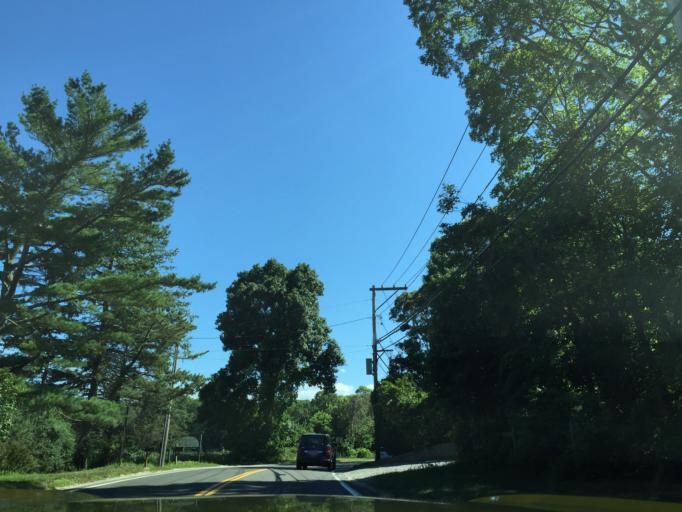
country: US
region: New York
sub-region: Suffolk County
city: North Sea
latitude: 40.9514
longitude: -72.3942
